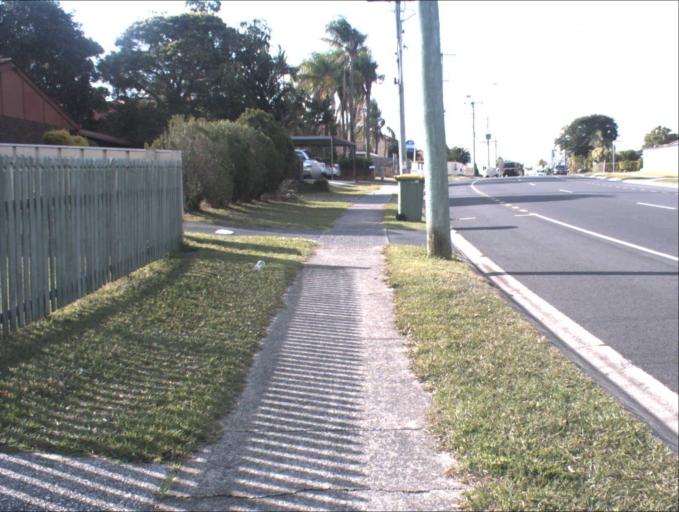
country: AU
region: Queensland
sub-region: Logan
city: Park Ridge South
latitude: -27.6719
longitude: 153.0370
